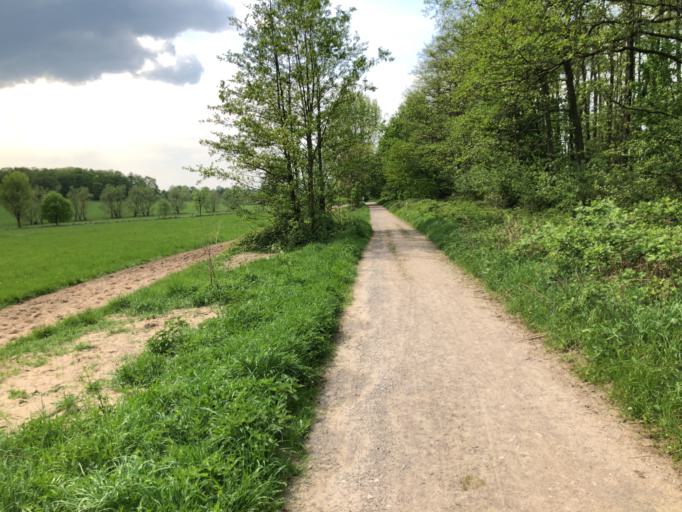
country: DE
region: North Rhine-Westphalia
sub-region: Regierungsbezirk Dusseldorf
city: Muelheim (Ruhr)
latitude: 51.3791
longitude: 6.8851
